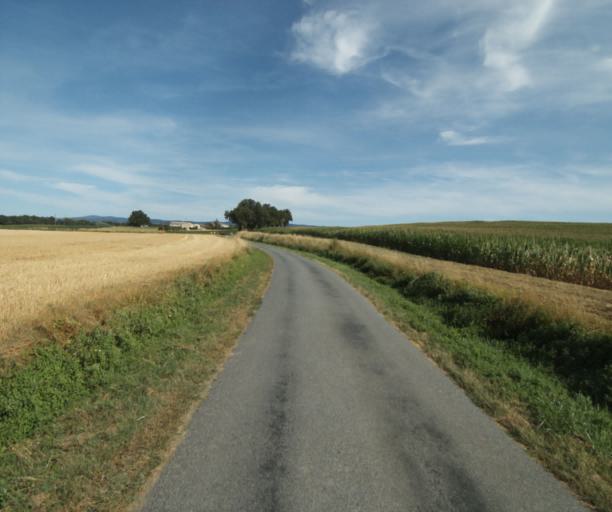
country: FR
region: Midi-Pyrenees
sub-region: Departement de la Haute-Garonne
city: Revel
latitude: 43.5127
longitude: 2.0409
